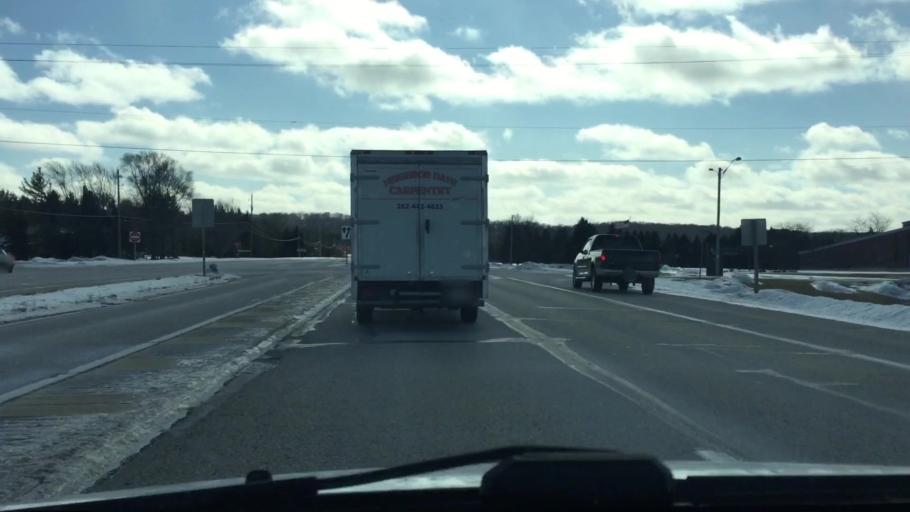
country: US
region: Wisconsin
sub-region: Waukesha County
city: Waukesha
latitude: 42.9490
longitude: -88.2283
